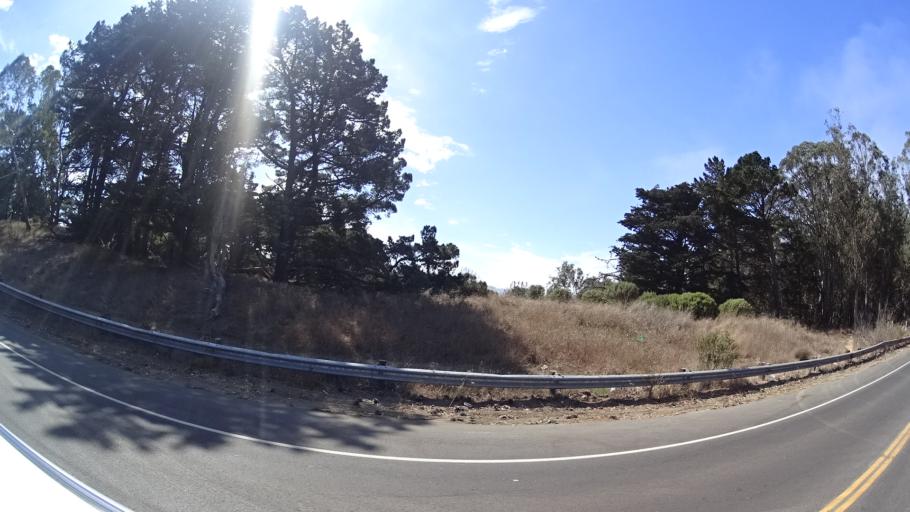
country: US
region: California
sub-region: San Mateo County
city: Brisbane
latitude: 37.7184
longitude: -122.4168
